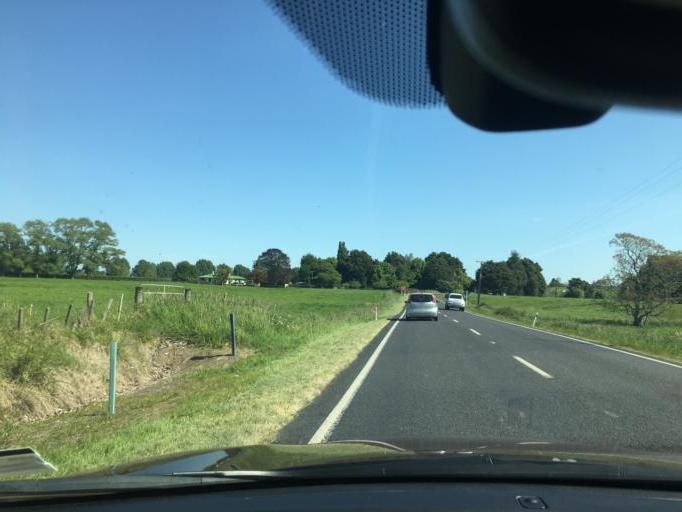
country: NZ
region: Waikato
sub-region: Waipa District
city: Cambridge
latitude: -37.9944
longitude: 175.3984
